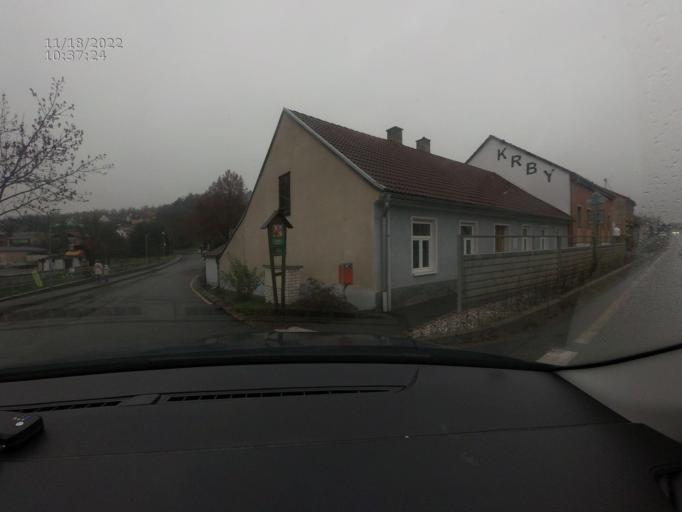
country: CZ
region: Central Bohemia
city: Zebrak
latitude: 49.8772
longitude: 13.9005
